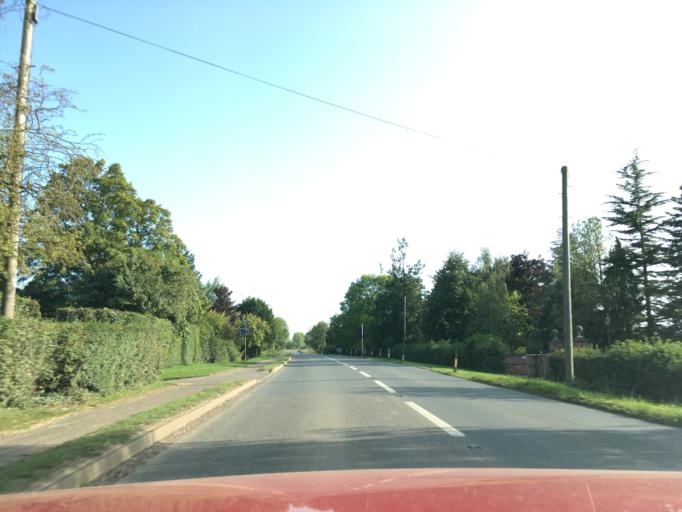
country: GB
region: England
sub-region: Gloucestershire
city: Newent
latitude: 51.9554
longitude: -2.3041
